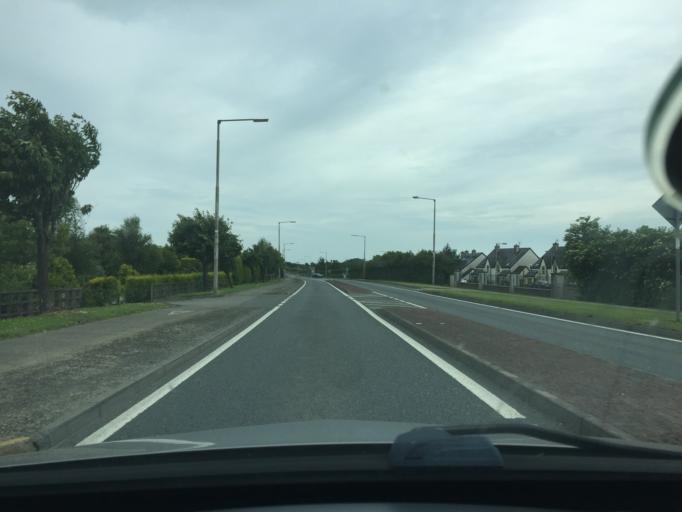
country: IE
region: Leinster
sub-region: Loch Garman
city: Enniscorthy
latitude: 52.4217
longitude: -6.5291
